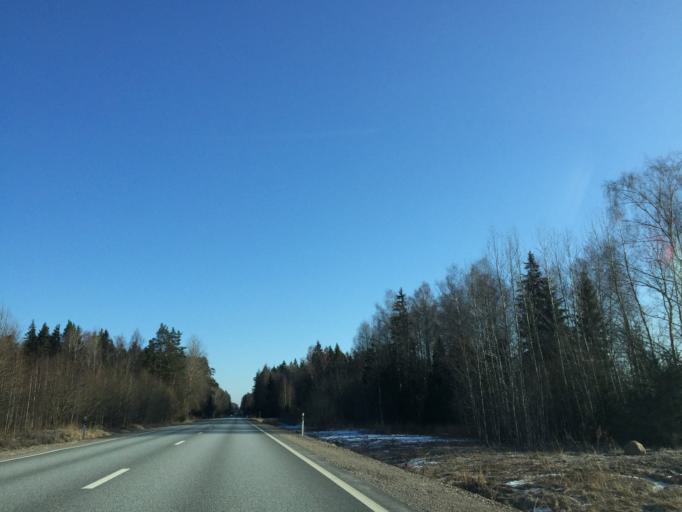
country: LV
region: Koceni
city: Koceni
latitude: 57.4794
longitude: 25.2914
